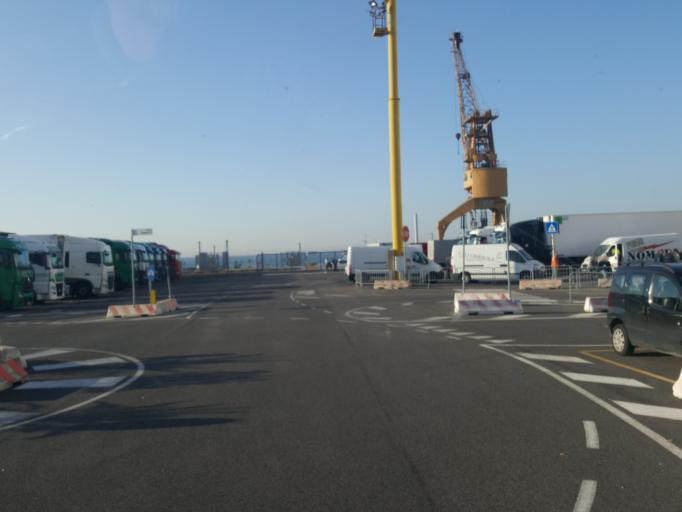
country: IT
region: Veneto
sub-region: Provincia di Venezia
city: Giudecca
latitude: 45.4331
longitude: 12.3095
